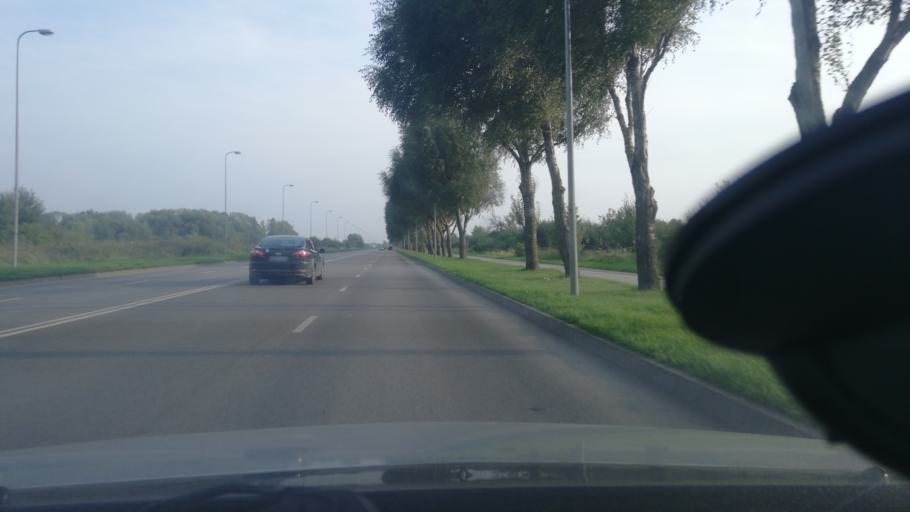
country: LT
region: Klaipedos apskritis
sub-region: Klaipeda
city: Klaipeda
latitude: 55.6609
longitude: 21.1670
